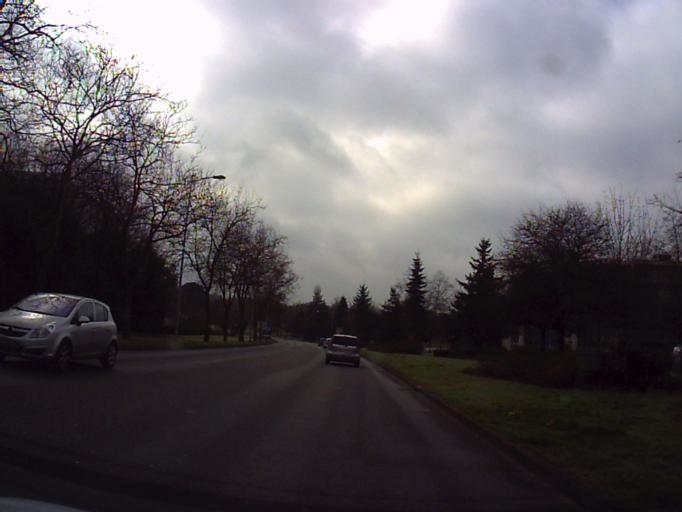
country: FR
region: Brittany
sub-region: Departement du Morbihan
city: Vannes
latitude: 47.6490
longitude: -2.7825
